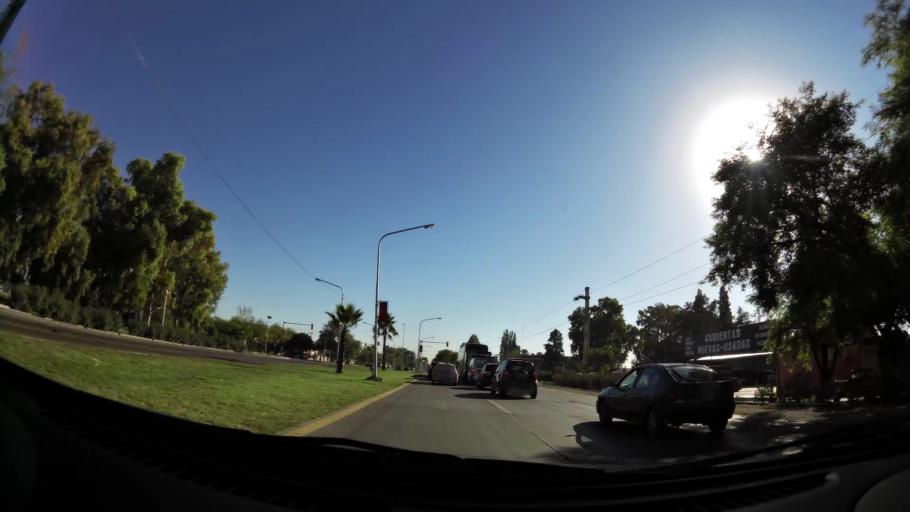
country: AR
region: Mendoza
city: Las Heras
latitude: -32.8681
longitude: -68.8134
